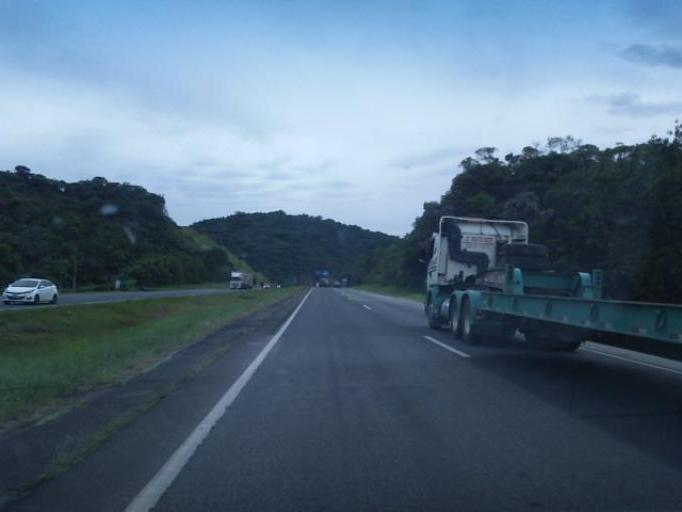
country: BR
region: Sao Paulo
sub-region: Juquia
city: Juquia
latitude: -24.3780
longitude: -47.7109
